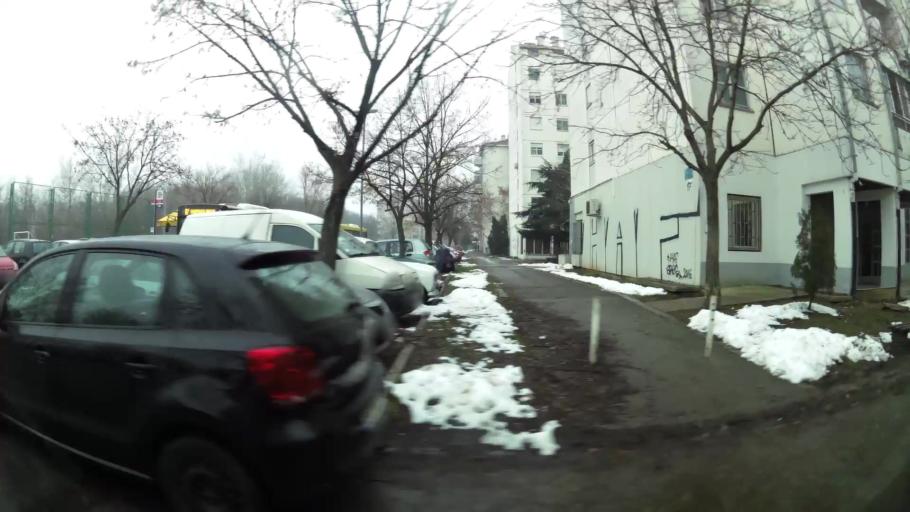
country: RS
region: Central Serbia
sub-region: Belgrade
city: Cukarica
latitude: 44.7778
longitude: 20.4047
